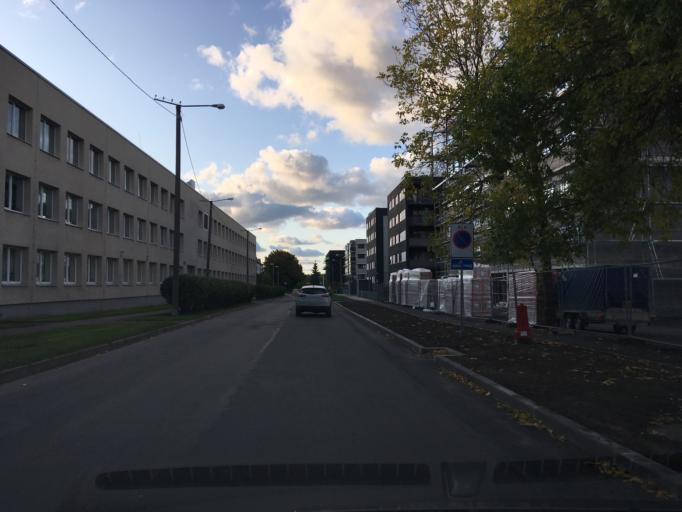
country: EE
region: Harju
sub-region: Tallinna linn
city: Tallinn
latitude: 59.4368
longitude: 24.8079
